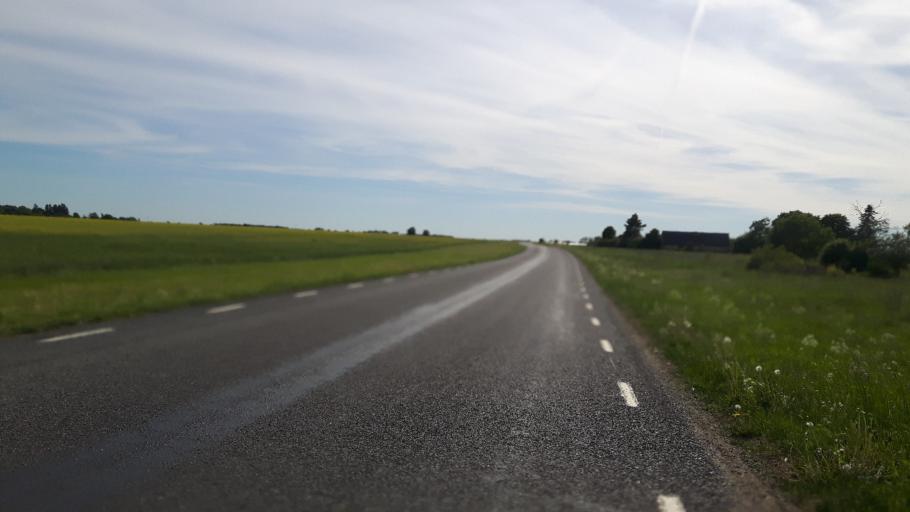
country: EE
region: Harju
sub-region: Raasiku vald
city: Raasiku
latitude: 59.4385
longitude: 25.1293
